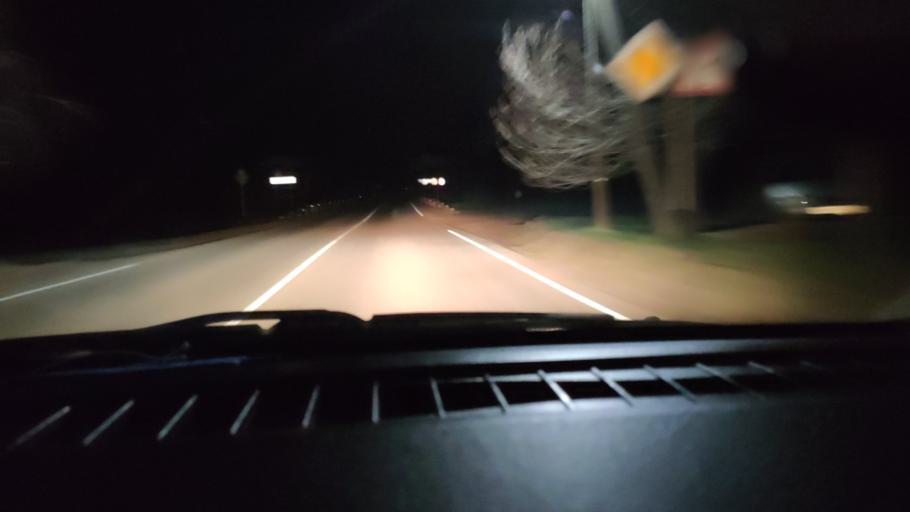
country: RU
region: Saratov
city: Privolzhskiy
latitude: 51.1896
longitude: 45.9157
